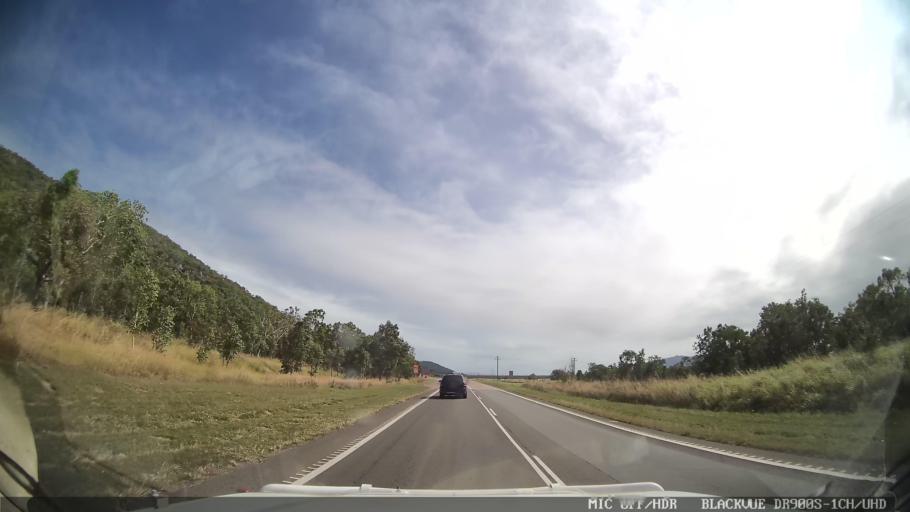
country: AU
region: Queensland
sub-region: Townsville
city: Townsville
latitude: -19.3995
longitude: 147.0243
